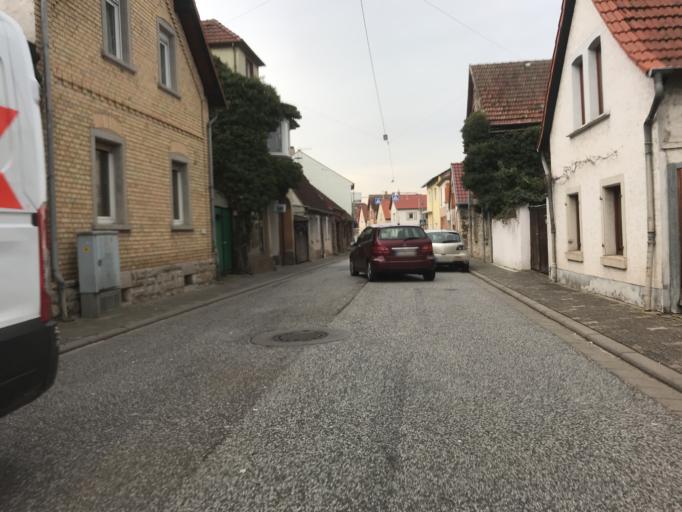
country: DE
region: Rheinland-Pfalz
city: Wackernheim
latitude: 49.9968
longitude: 8.1202
